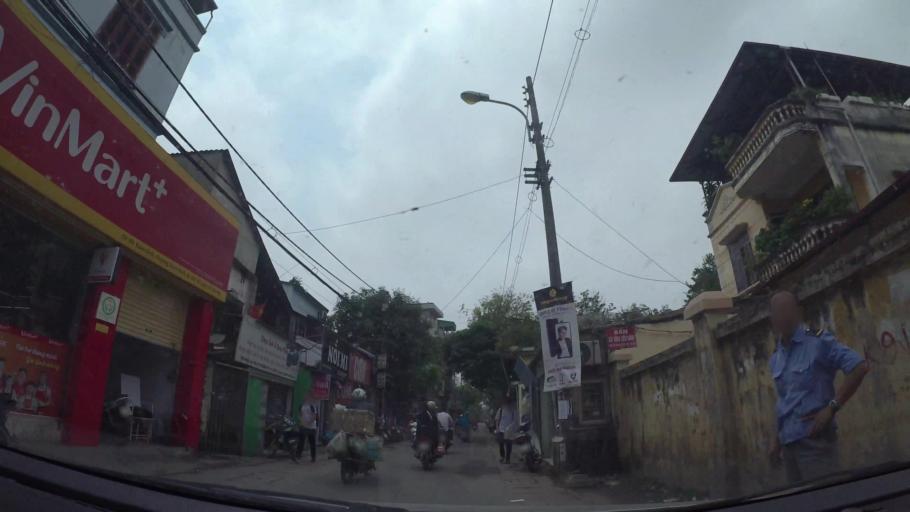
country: VN
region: Ha Noi
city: Tay Ho
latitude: 21.0711
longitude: 105.7961
